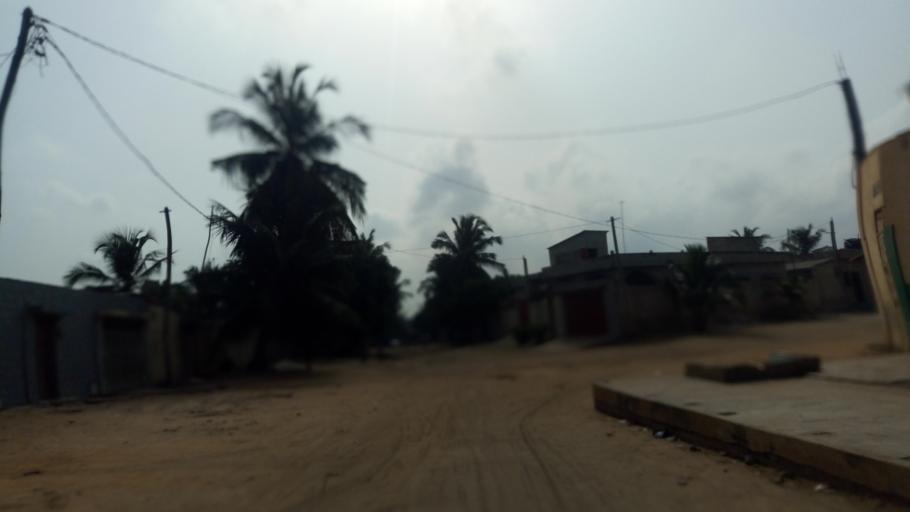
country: TG
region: Maritime
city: Lome
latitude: 6.1783
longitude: 1.1719
